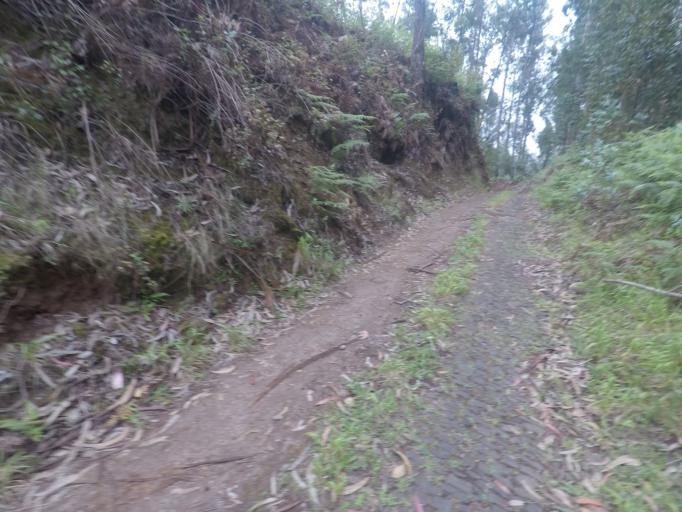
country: PT
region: Madeira
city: Ponta do Sol
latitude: 32.7221
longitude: -17.0924
